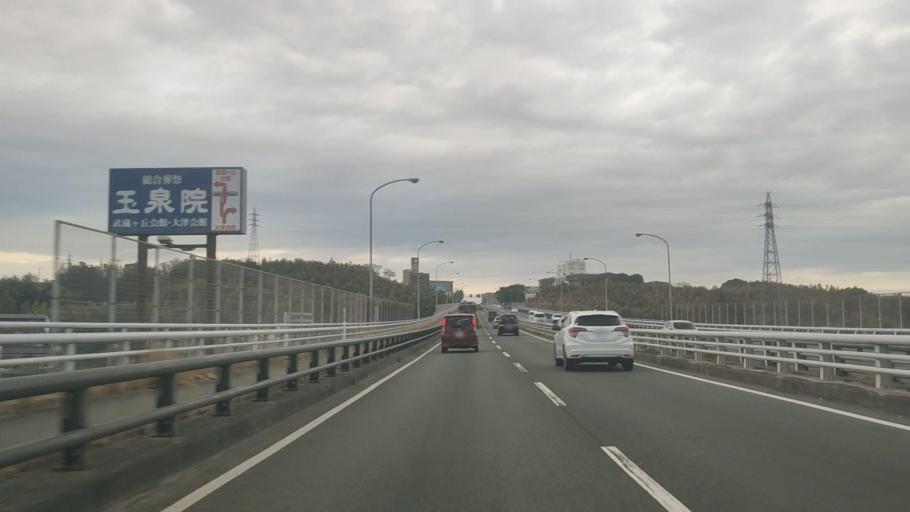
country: JP
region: Kumamoto
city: Ozu
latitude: 32.8468
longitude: 130.7818
